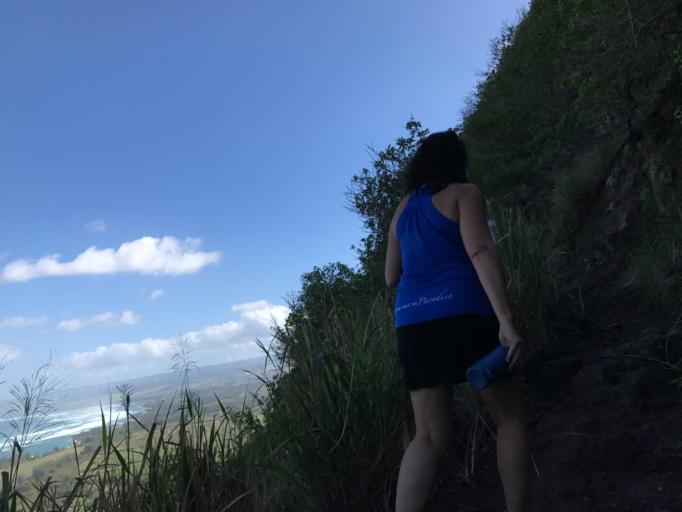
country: US
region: Hawaii
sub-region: Honolulu County
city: Mokuleia
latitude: 21.5722
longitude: -158.2092
